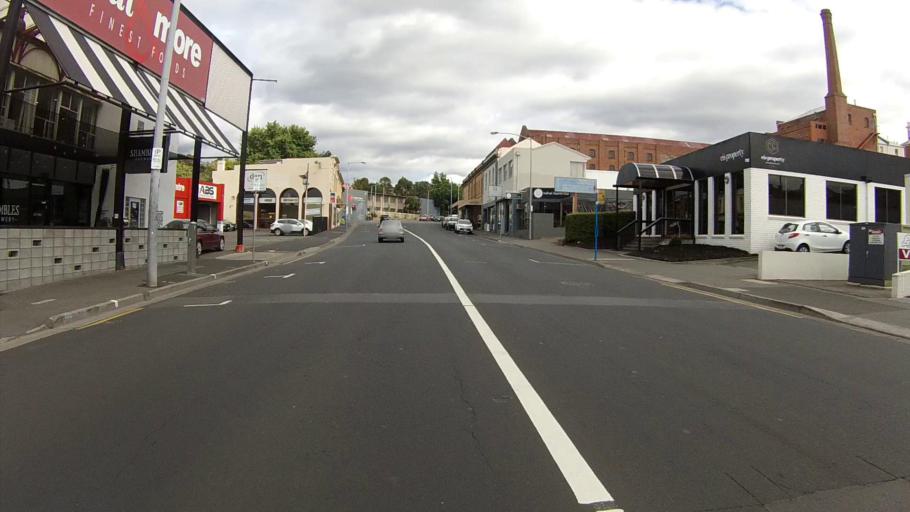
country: AU
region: Tasmania
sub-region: Hobart
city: Hobart
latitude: -42.8784
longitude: 147.3206
